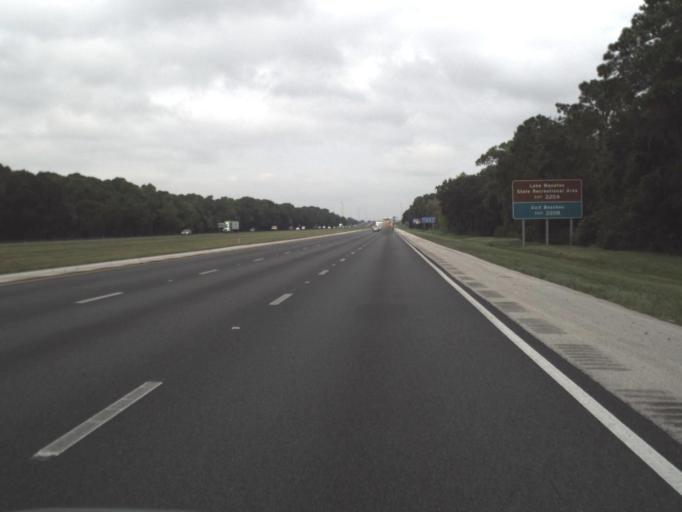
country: US
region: Florida
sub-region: Manatee County
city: Samoset
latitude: 27.4752
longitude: -82.4641
